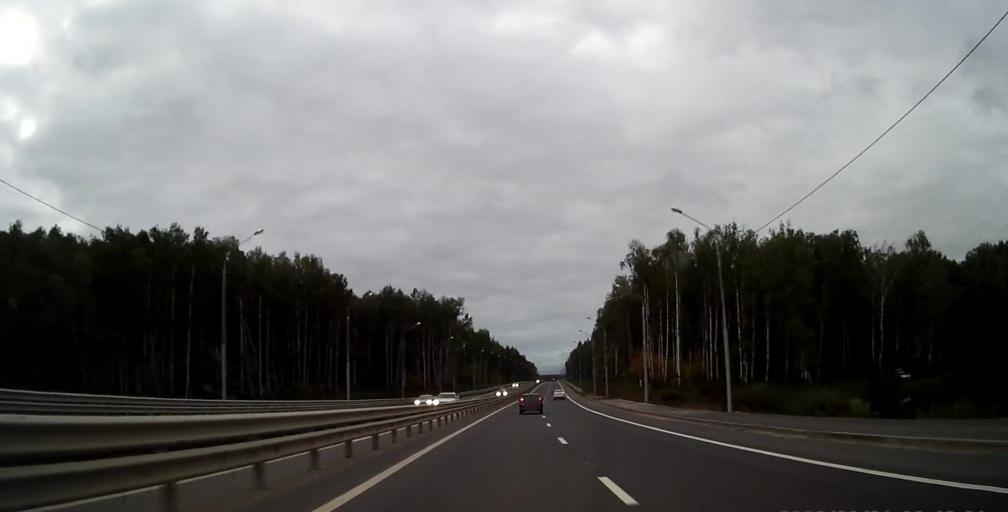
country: RU
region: Moskovskaya
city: Klimovsk
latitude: 55.3815
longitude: 37.5251
